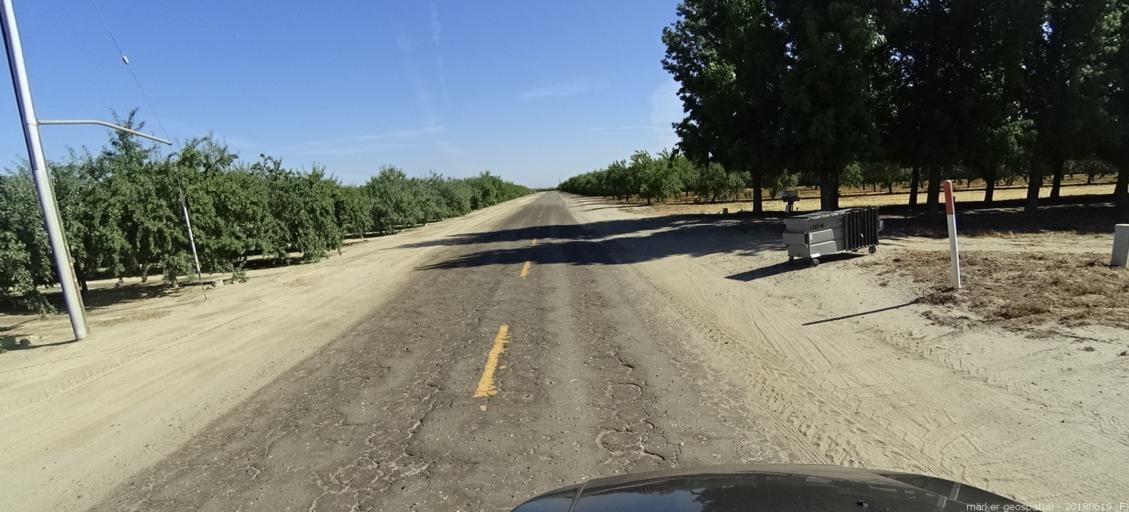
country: US
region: California
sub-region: Fresno County
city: Biola
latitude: 36.8323
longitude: -120.0428
